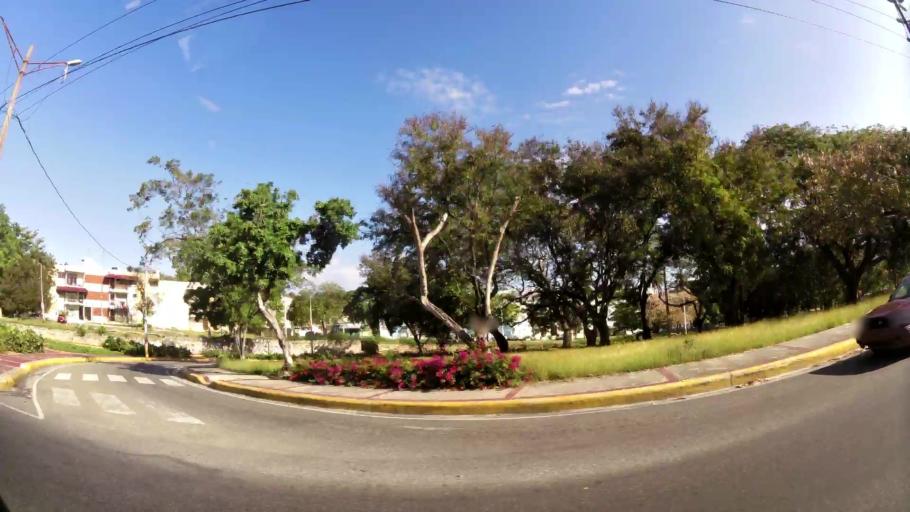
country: DO
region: Nacional
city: San Carlos
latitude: 18.4819
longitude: -69.8785
